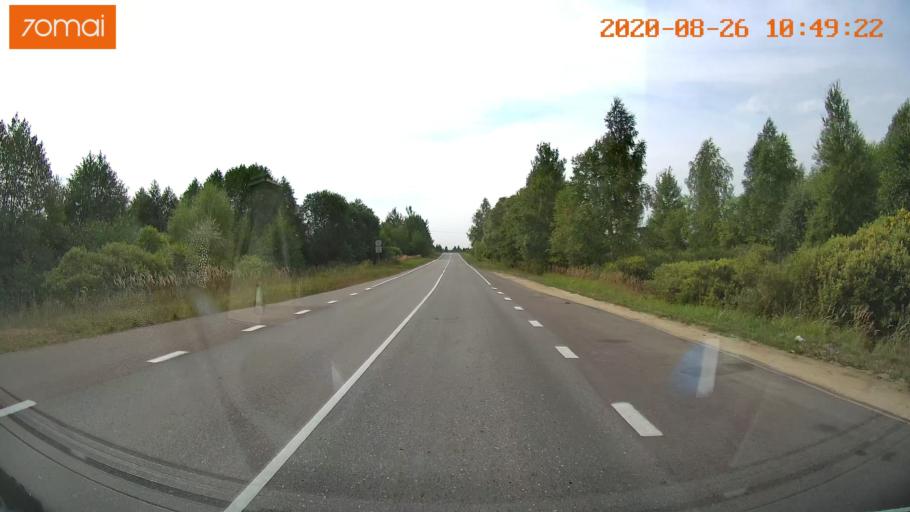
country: RU
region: Rjazan
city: Lashma
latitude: 54.7036
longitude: 41.1606
